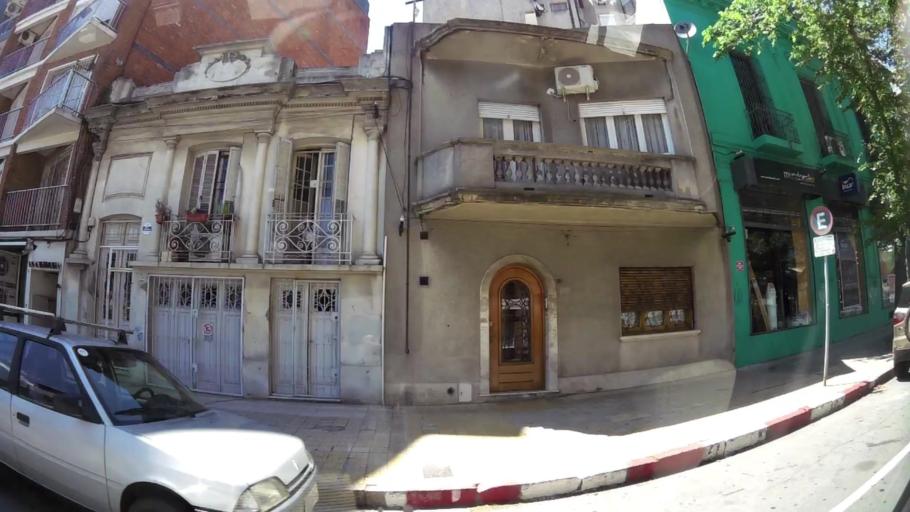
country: UY
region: Montevideo
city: Montevideo
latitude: -34.9071
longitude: -56.1744
